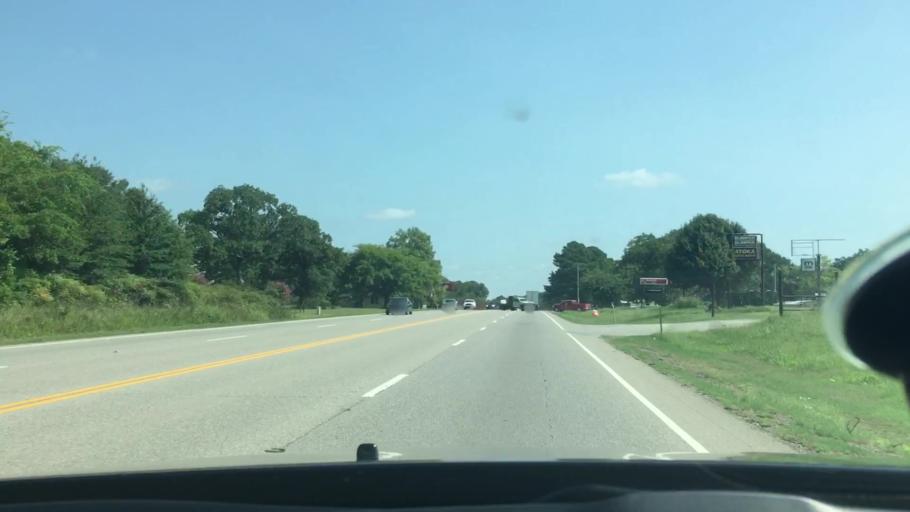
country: US
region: Oklahoma
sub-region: Atoka County
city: Atoka
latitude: 34.3391
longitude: -96.1553
